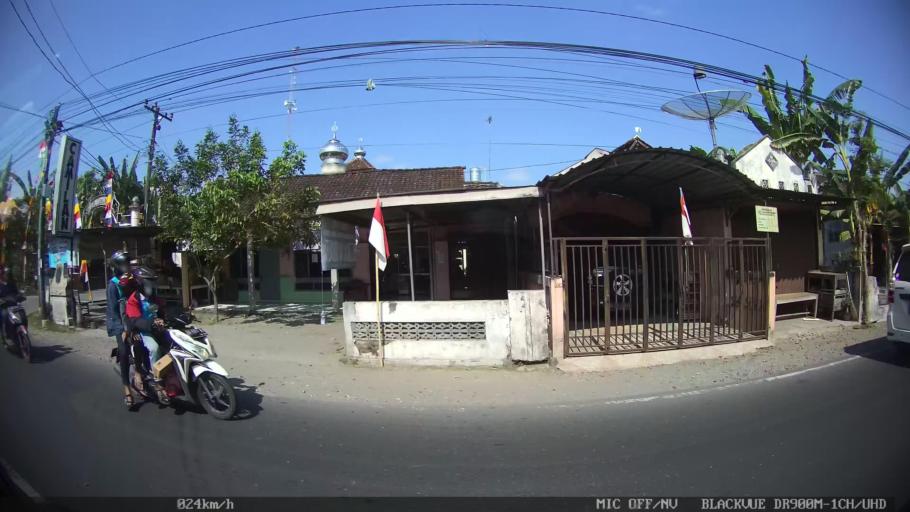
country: ID
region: Daerah Istimewa Yogyakarta
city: Sewon
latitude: -7.8815
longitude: 110.3895
